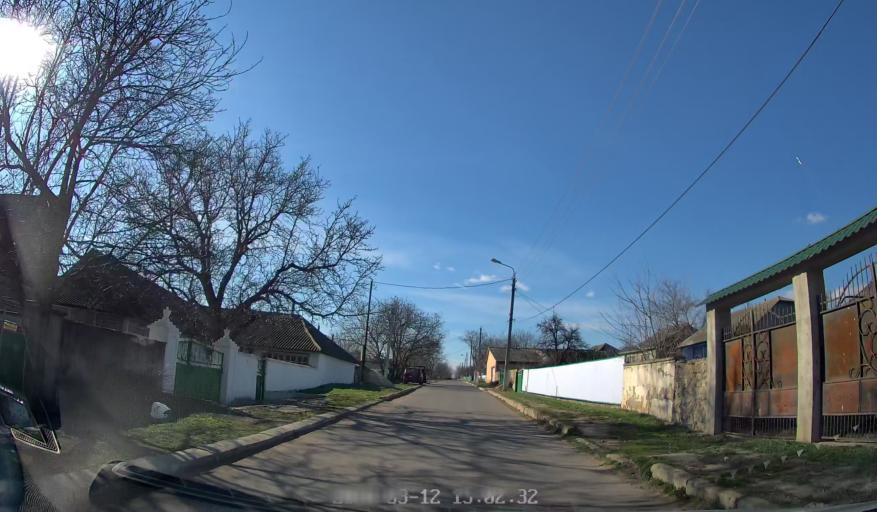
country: MD
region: Telenesti
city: Cocieri
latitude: 47.2227
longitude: 29.0259
